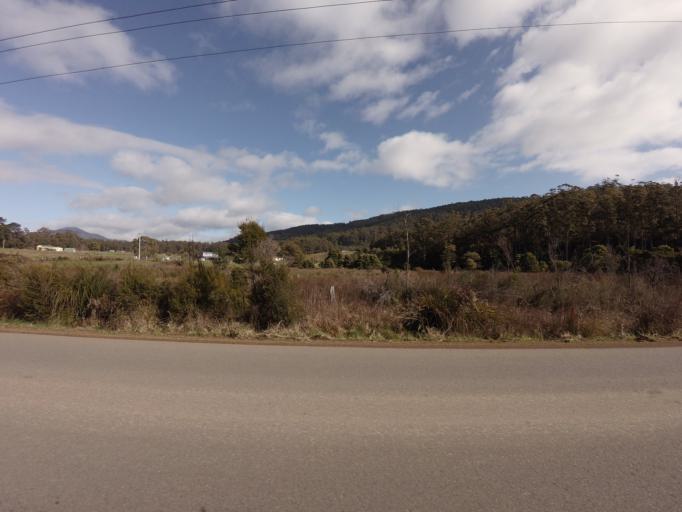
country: AU
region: Tasmania
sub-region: Huon Valley
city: Geeveston
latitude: -43.3270
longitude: 146.9714
